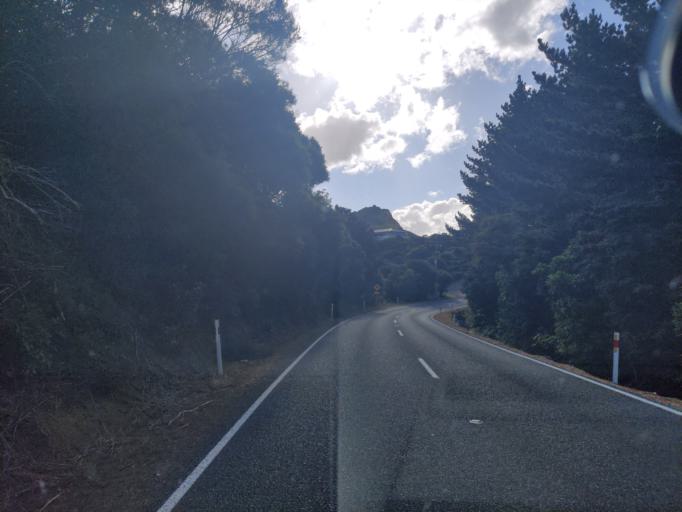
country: NZ
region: Northland
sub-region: Whangarei
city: Ngunguru
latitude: -35.6168
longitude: 174.5219
